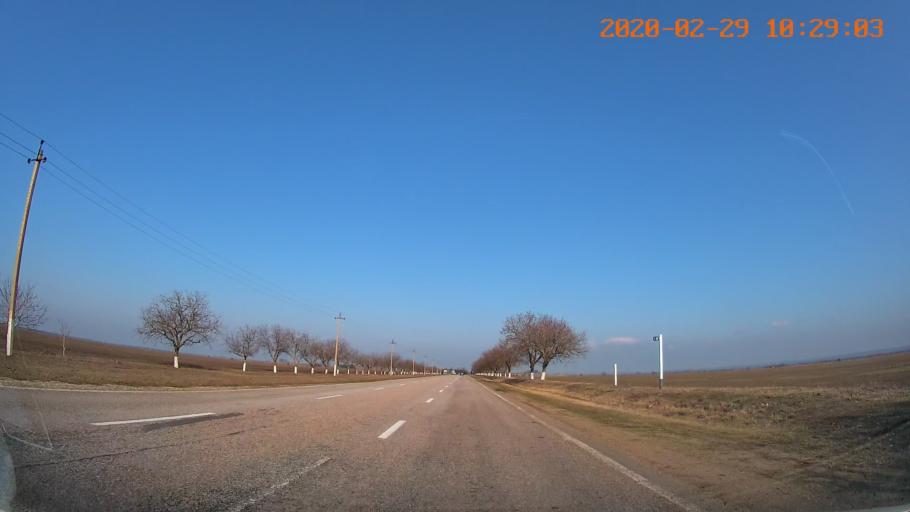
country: MD
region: Telenesti
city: Tiraspolul Nou
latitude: 46.9188
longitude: 29.5878
